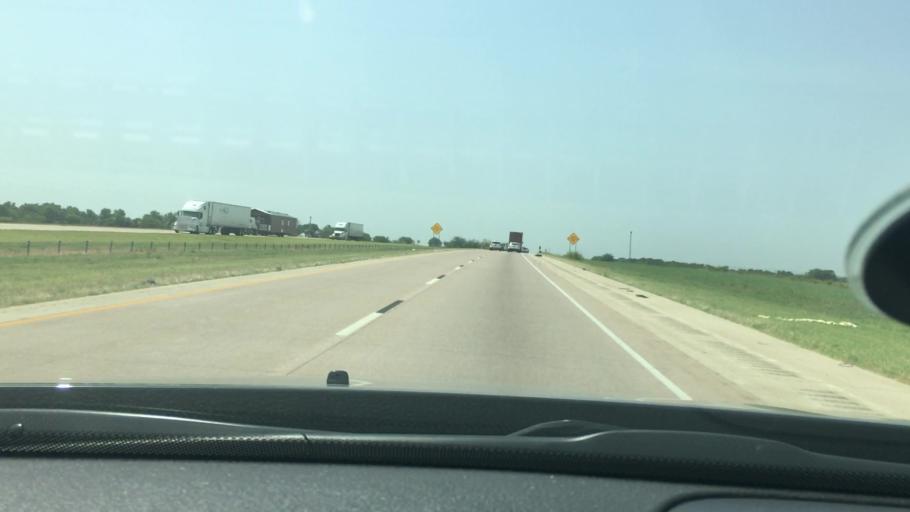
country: US
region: Oklahoma
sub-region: Garvin County
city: Pauls Valley
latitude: 34.6841
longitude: -97.2294
